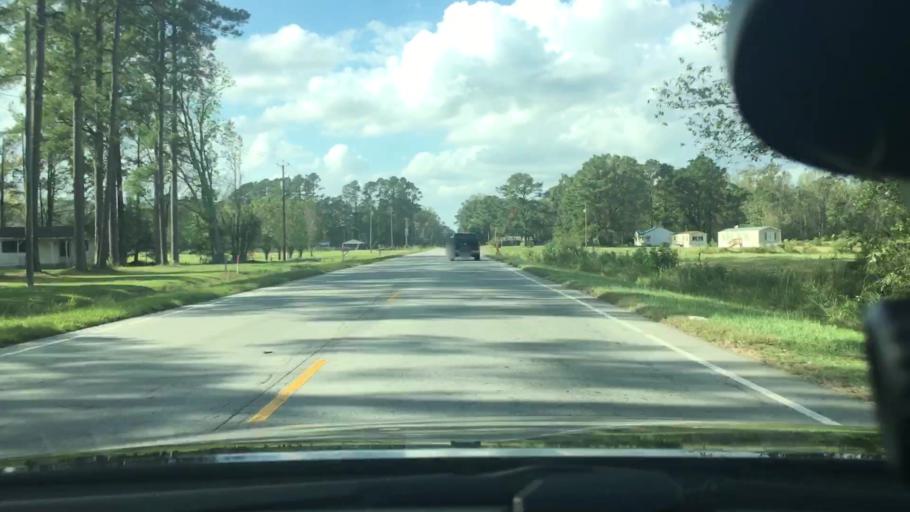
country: US
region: North Carolina
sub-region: Craven County
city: Vanceboro
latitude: 35.2557
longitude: -77.0954
